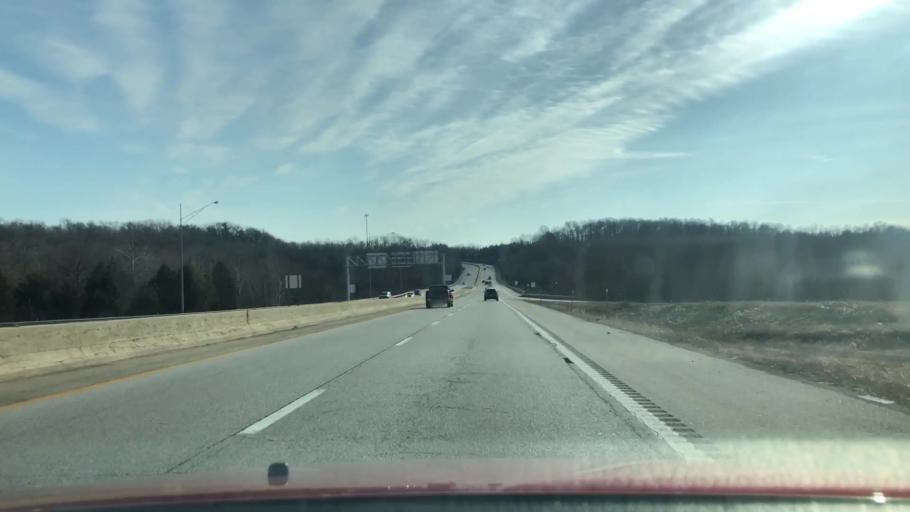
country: US
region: Missouri
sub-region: Christian County
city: Nixa
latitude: 37.1267
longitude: -93.2291
